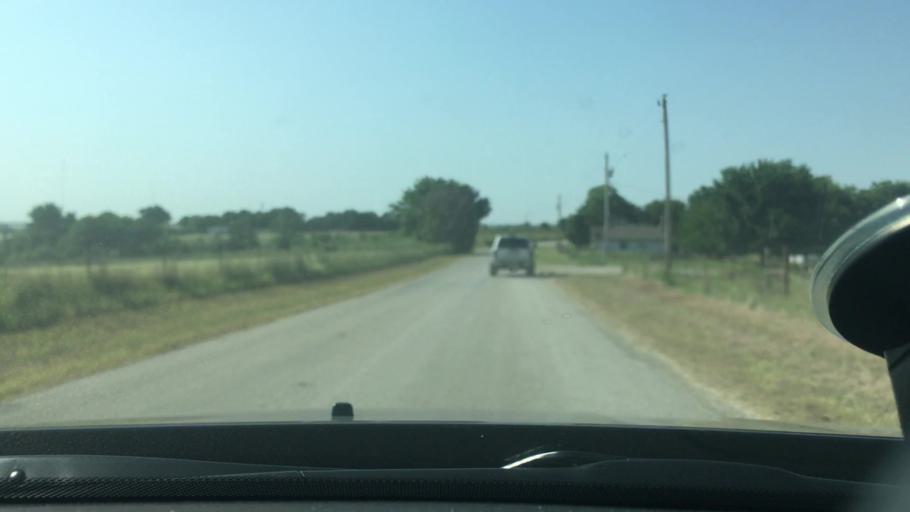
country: US
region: Oklahoma
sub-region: Garvin County
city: Lindsay
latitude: 34.7805
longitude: -97.6095
